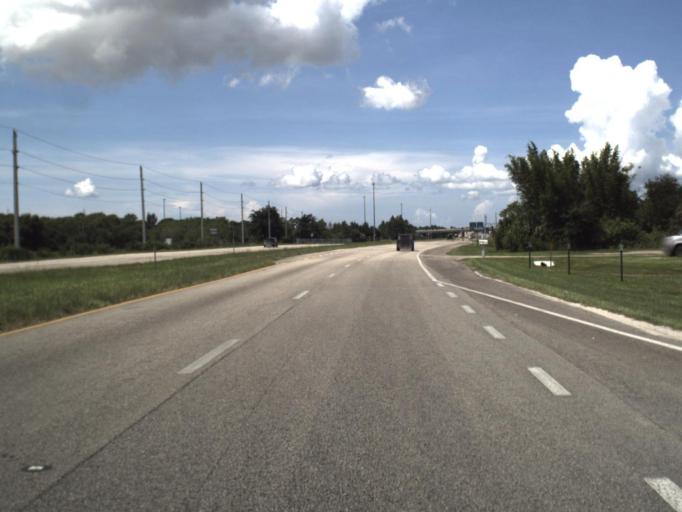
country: US
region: Florida
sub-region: Charlotte County
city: Cleveland
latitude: 26.9432
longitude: -82.0113
